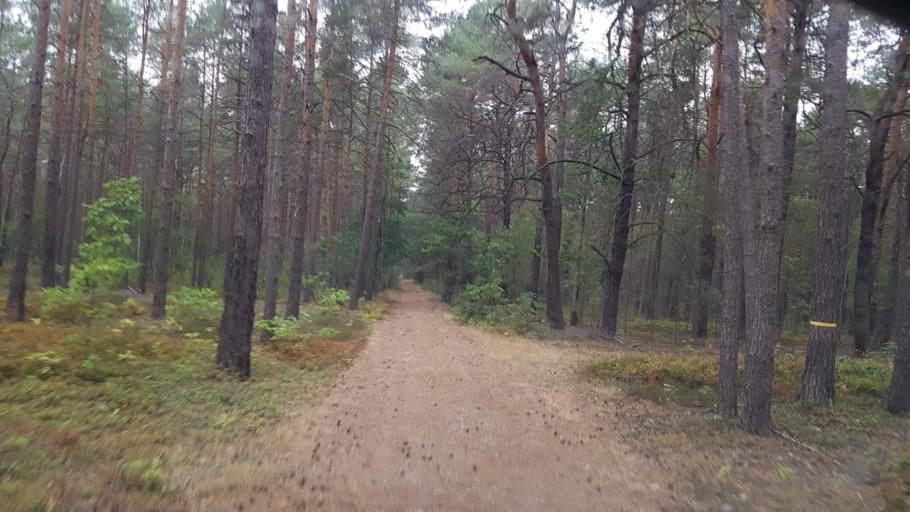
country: DE
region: Brandenburg
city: Sallgast
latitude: 51.6026
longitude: 13.8307
